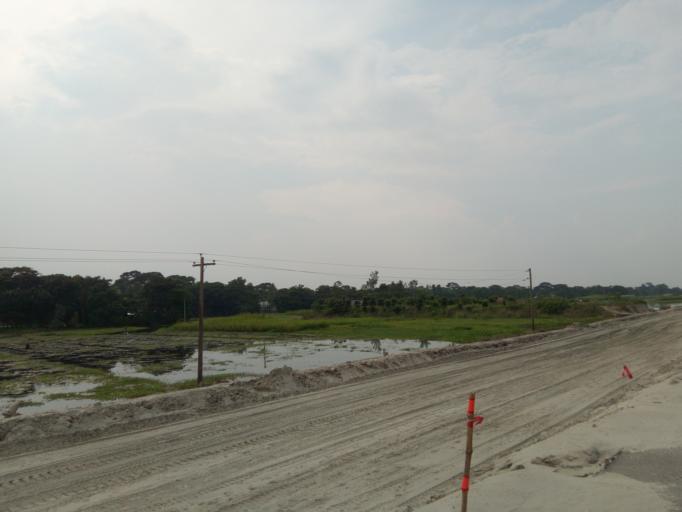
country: BD
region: Dhaka
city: Dohar
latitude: 23.5598
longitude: 90.2989
